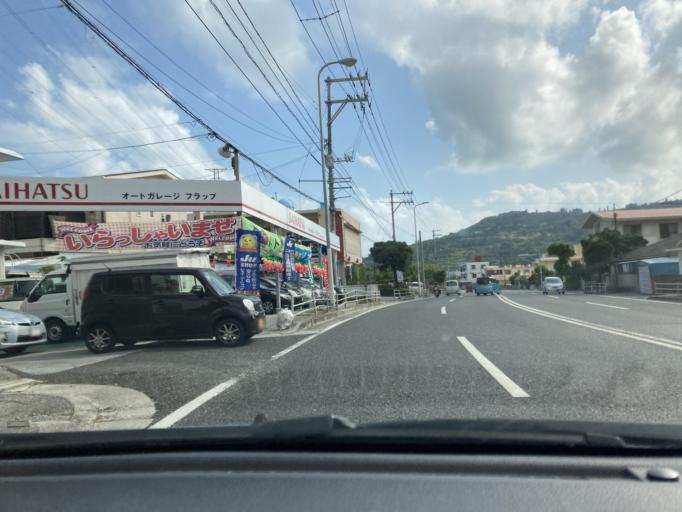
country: JP
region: Okinawa
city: Okinawa
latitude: 26.2982
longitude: 127.8090
